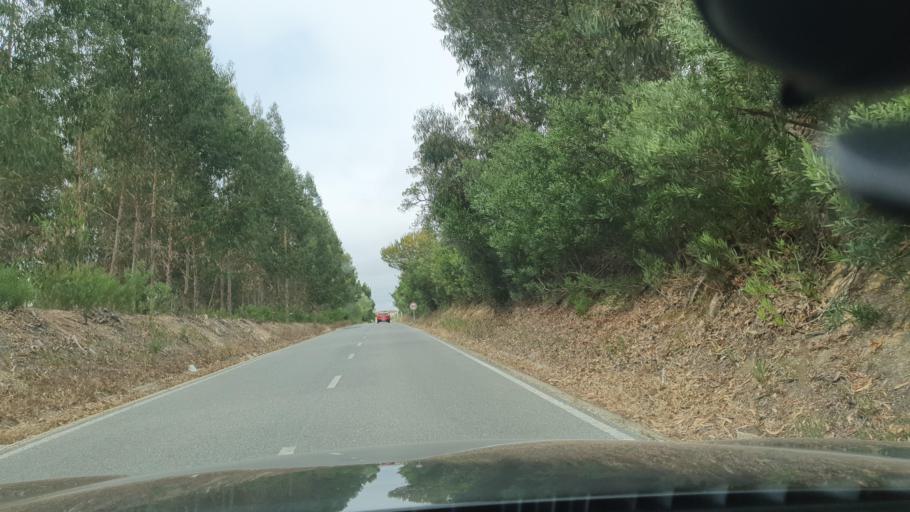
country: PT
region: Beja
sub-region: Odemira
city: Sao Teotonio
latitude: 37.5430
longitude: -8.7484
